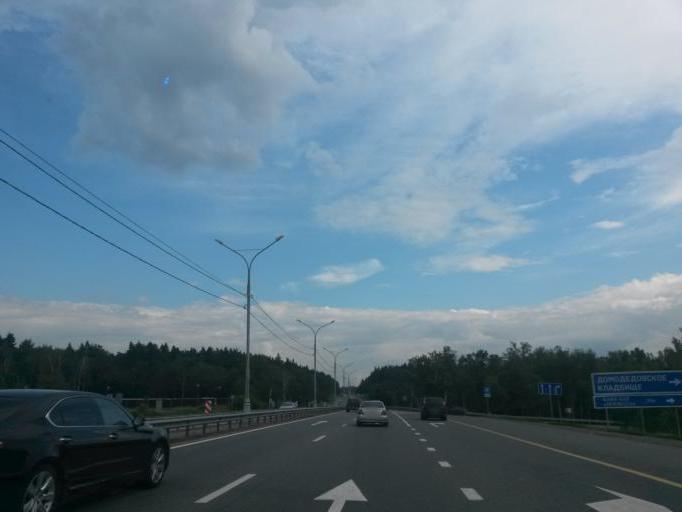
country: RU
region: Moskovskaya
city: Vostryakovo
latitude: 55.4529
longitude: 37.8573
